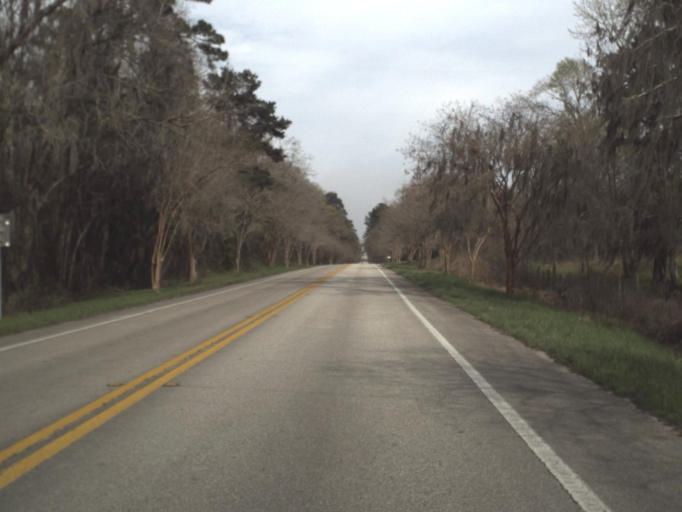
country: US
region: Florida
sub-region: Jefferson County
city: Monticello
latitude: 30.5346
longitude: -83.9442
